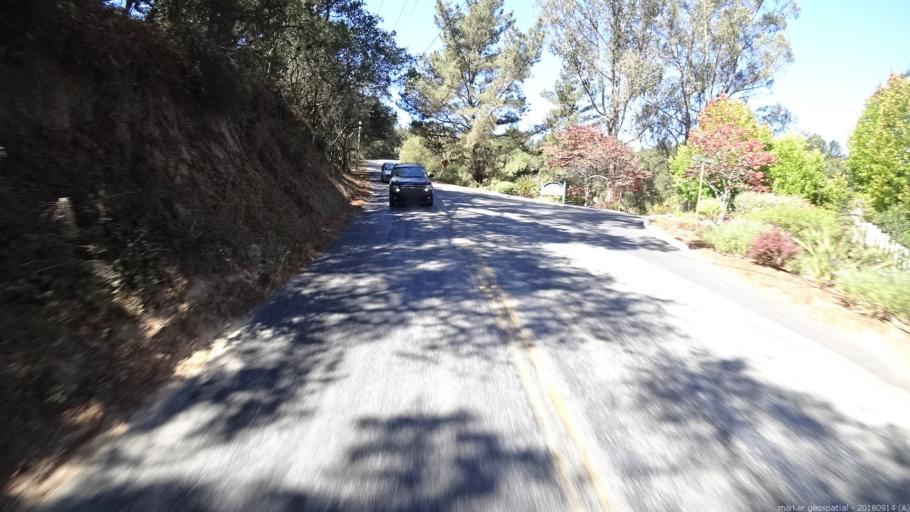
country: US
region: California
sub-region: Monterey County
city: Las Lomas
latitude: 36.8831
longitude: -121.6991
